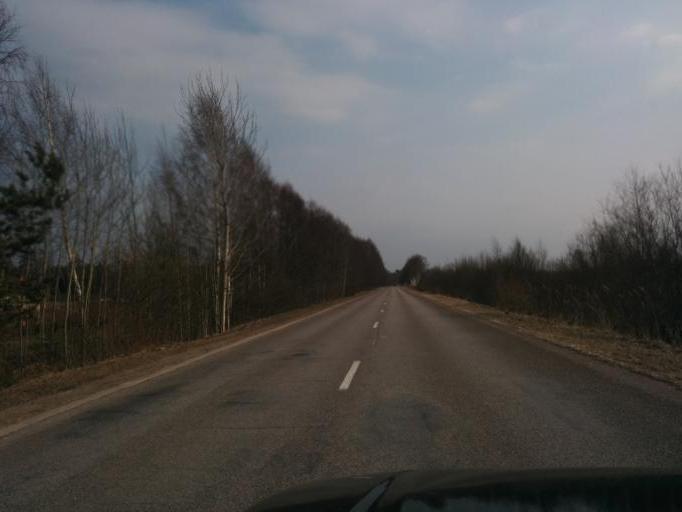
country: LV
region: Kekava
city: Balozi
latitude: 56.7811
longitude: 24.0989
